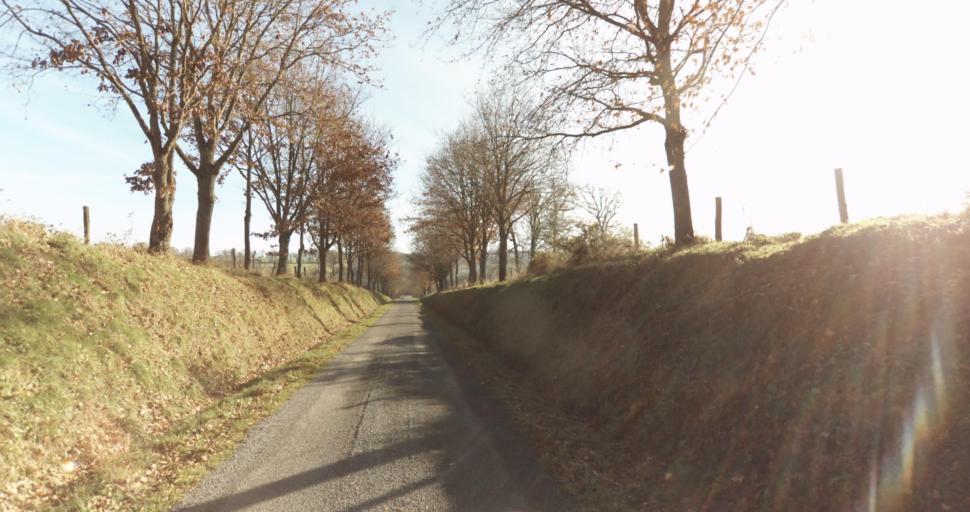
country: FR
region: Limousin
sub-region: Departement de la Haute-Vienne
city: Saint-Priest-sous-Aixe
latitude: 45.7863
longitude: 1.1063
